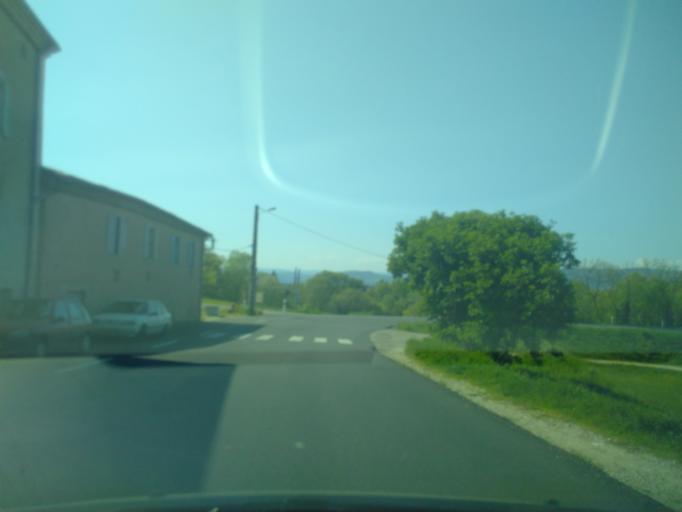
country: FR
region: Rhone-Alpes
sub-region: Departement de la Drome
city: La Begude-de-Mazenc
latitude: 44.5933
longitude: 4.9512
